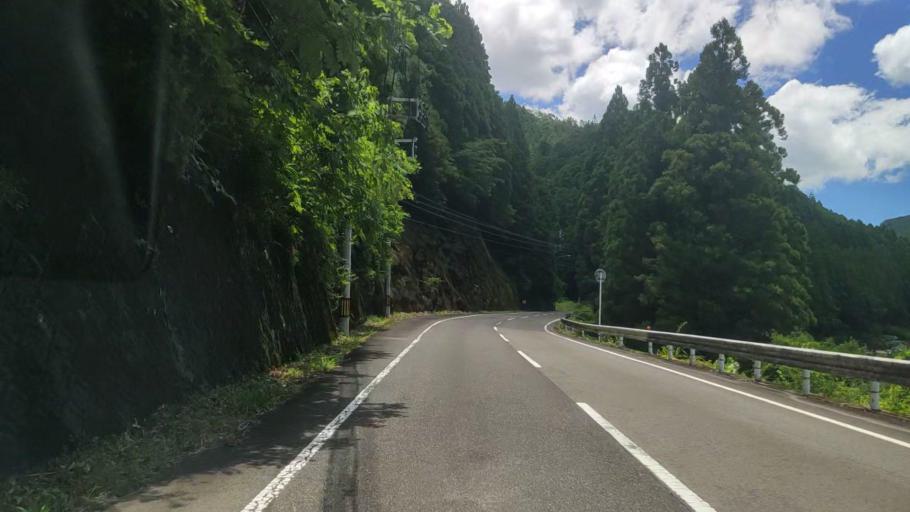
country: JP
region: Mie
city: Owase
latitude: 33.9700
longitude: 136.0613
